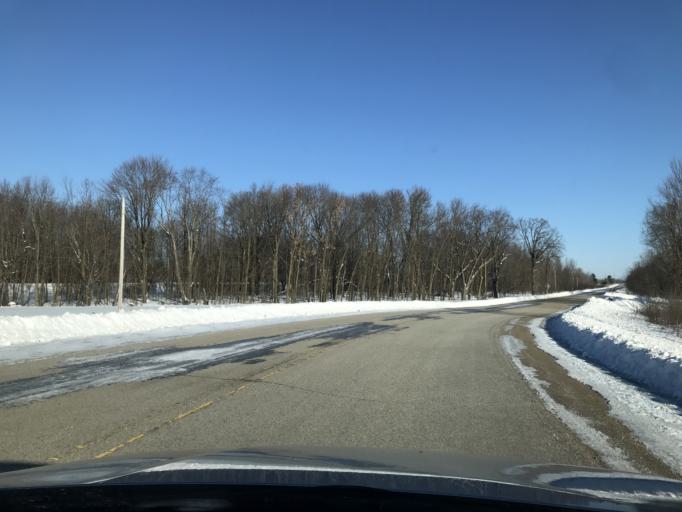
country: US
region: Wisconsin
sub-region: Oconto County
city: Oconto Falls
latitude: 44.9709
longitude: -88.0458
